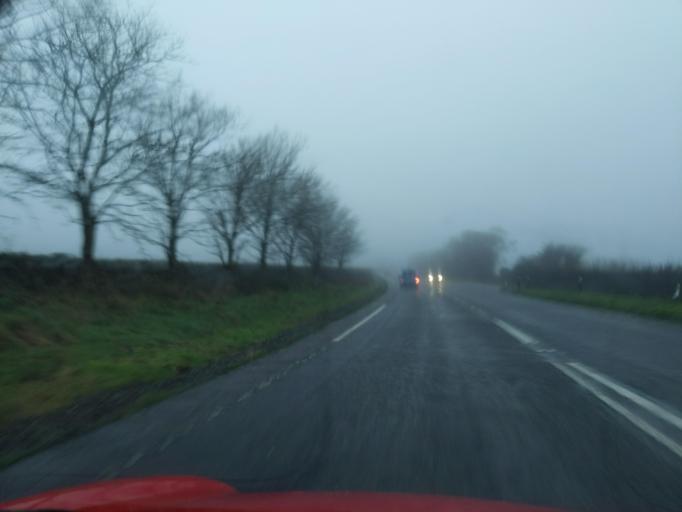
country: GB
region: England
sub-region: Cornwall
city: Callington
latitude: 50.4890
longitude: -4.2880
